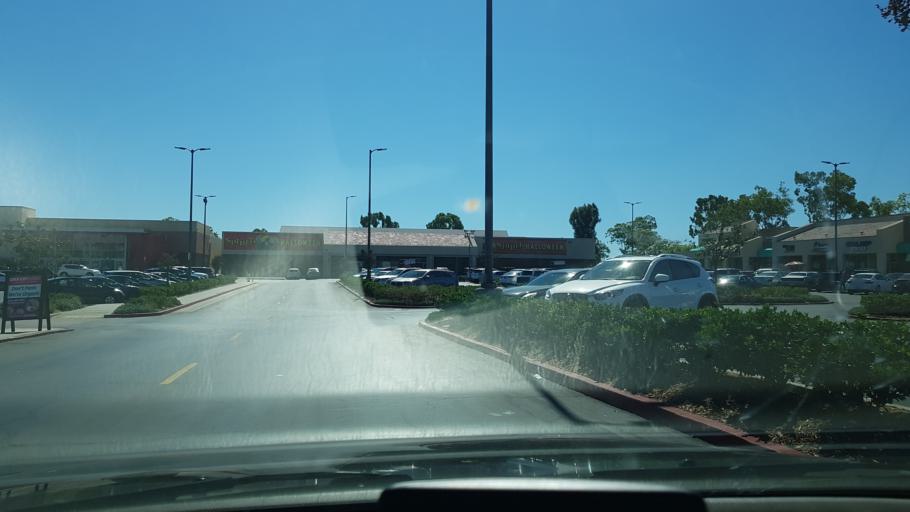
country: US
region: California
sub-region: San Diego County
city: Fairbanks Ranch
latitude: 32.9117
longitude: -117.1468
